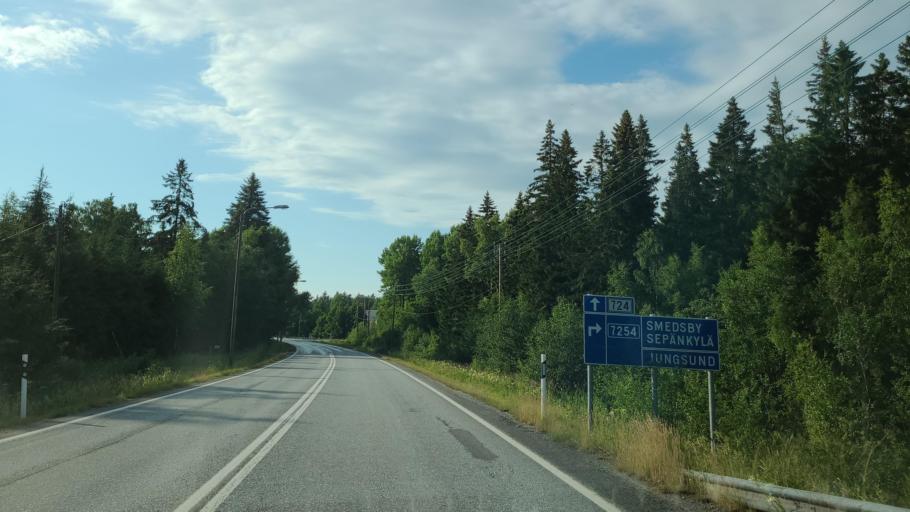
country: FI
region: Ostrobothnia
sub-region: Vaasa
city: Vaasa
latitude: 63.1907
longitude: 21.5635
